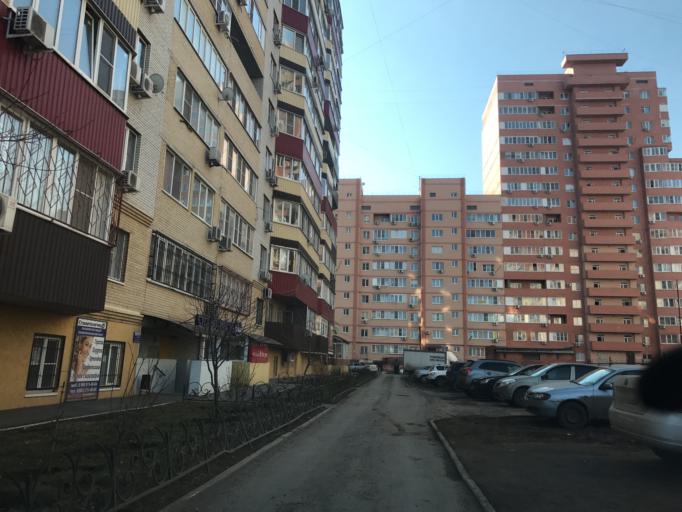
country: RU
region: Rostov
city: Rostov-na-Donu
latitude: 47.2165
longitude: 39.6195
